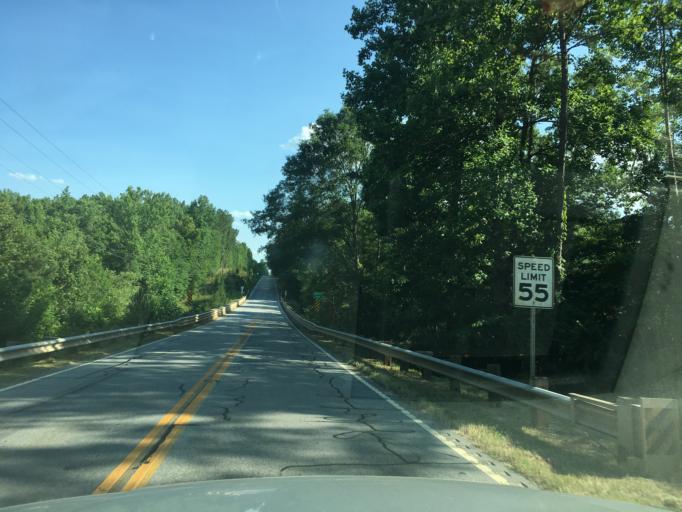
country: US
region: South Carolina
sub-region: Laurens County
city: Watts Mills
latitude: 34.6040
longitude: -81.9150
